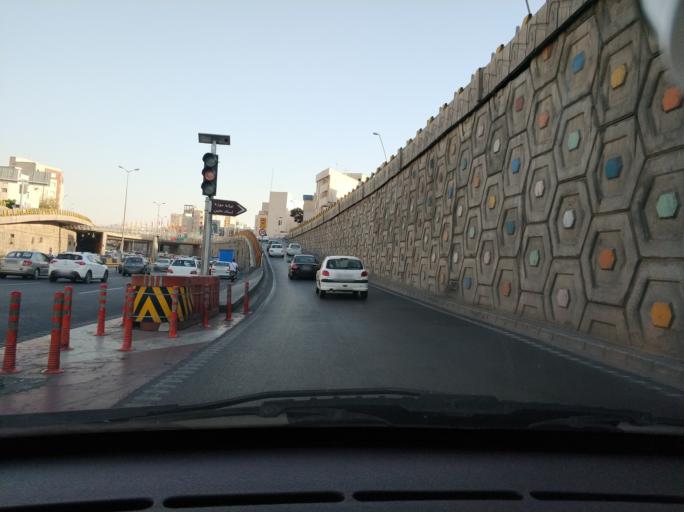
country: IR
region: Tehran
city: Tehran
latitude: 35.6895
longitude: 51.4569
